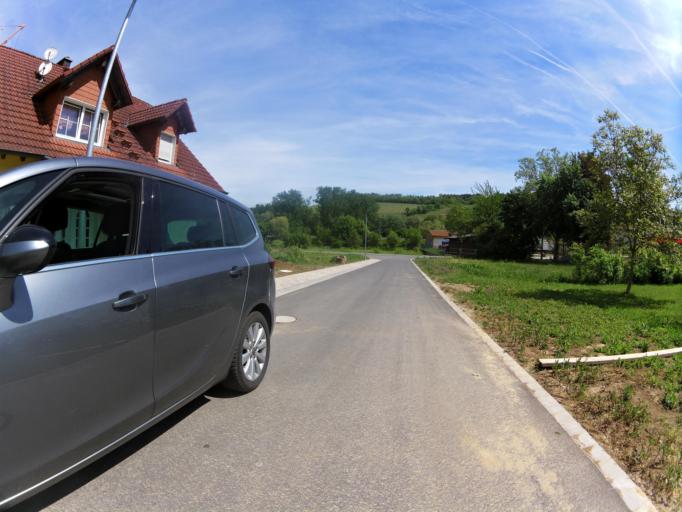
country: DE
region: Bavaria
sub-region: Regierungsbezirk Unterfranken
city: Sommerhausen
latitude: 49.6825
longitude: 10.0270
